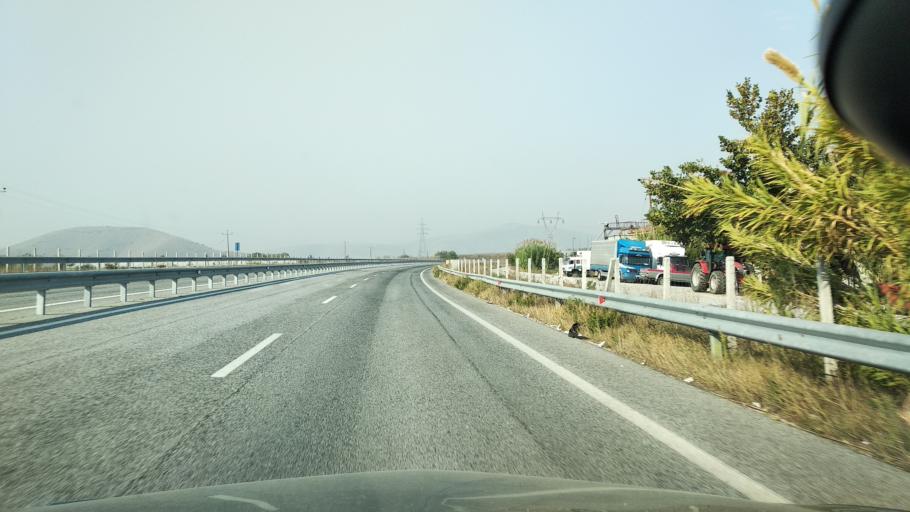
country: GR
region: Thessaly
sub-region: Trikala
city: Farkadona
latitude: 39.5829
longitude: 22.0548
